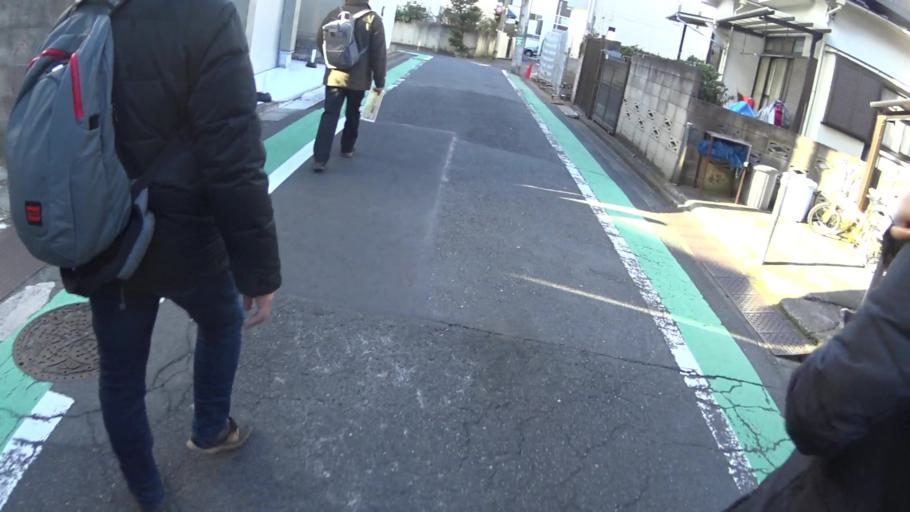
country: JP
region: Tokyo
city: Tokyo
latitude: 35.6783
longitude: 139.6888
